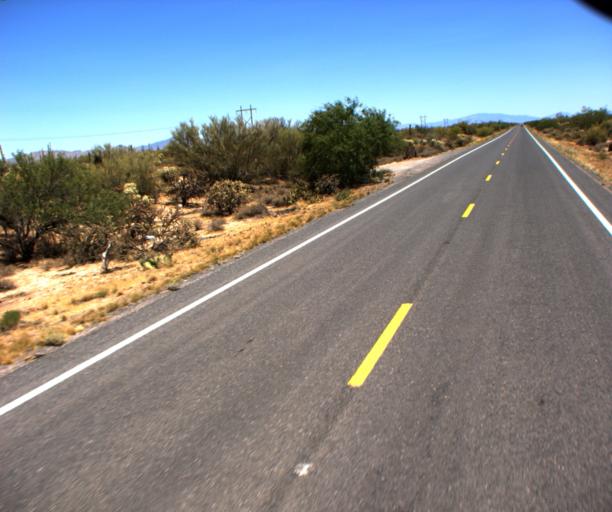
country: US
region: Arizona
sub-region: Pinal County
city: Florence
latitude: 32.8641
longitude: -111.2438
